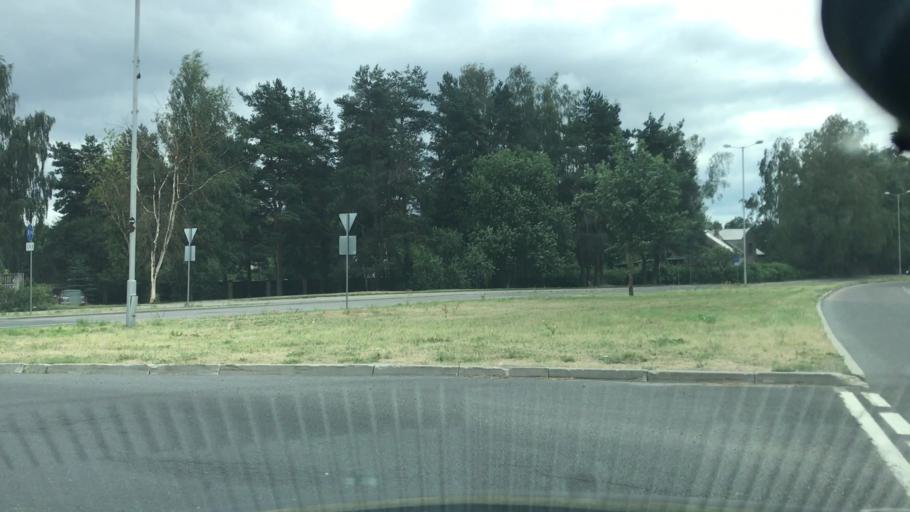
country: LV
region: Marupe
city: Marupe
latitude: 56.9574
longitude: 24.0235
